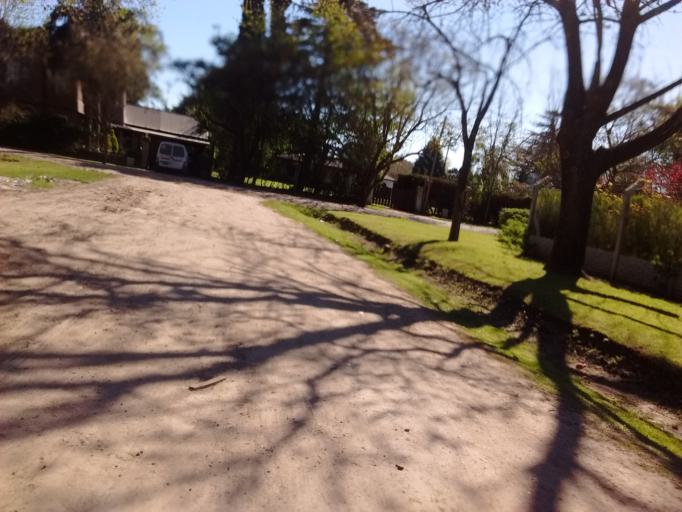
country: AR
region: Santa Fe
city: Funes
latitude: -32.9252
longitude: -60.8163
